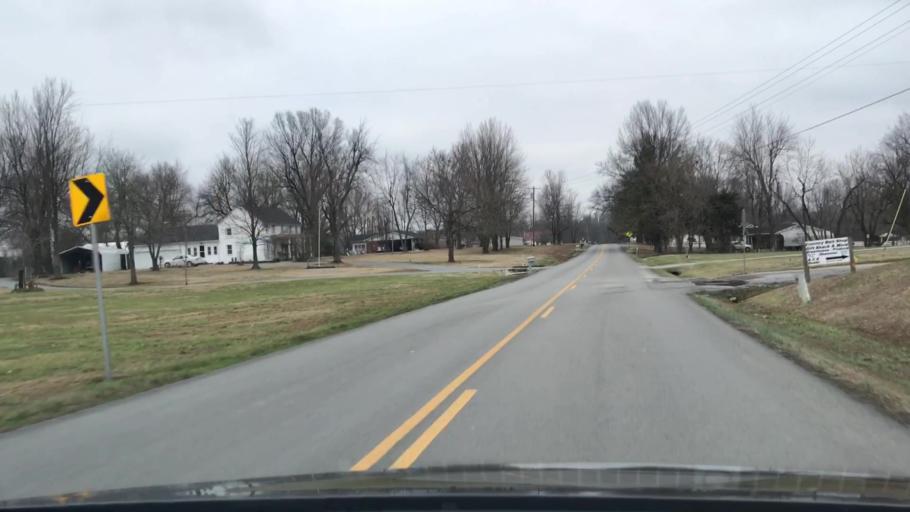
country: US
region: Kentucky
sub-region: Muhlenberg County
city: Morehead
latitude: 37.3397
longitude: -87.2217
